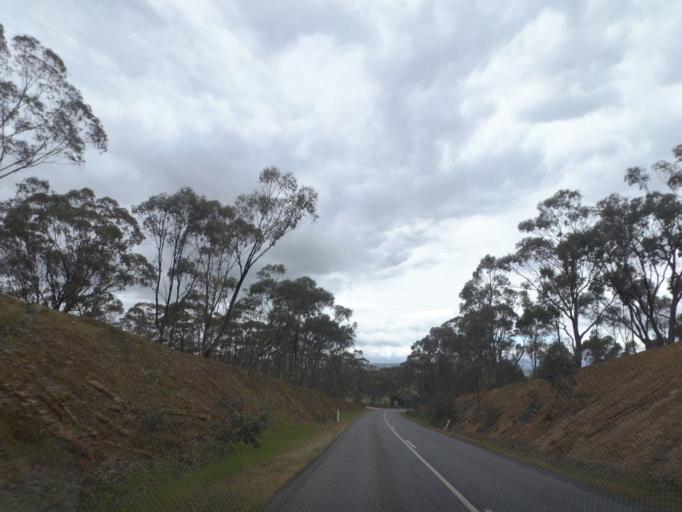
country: AU
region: Victoria
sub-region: Hume
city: Sunbury
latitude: -37.3969
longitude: 144.8425
